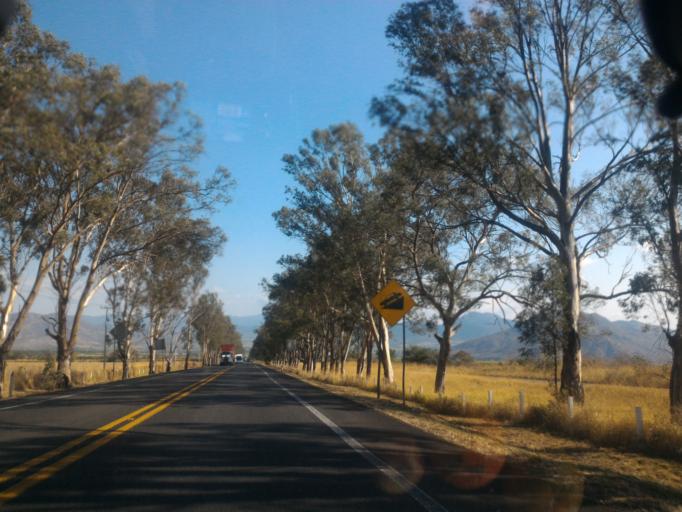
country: MX
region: Jalisco
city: Tuxpan
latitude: 19.5536
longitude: -103.4370
